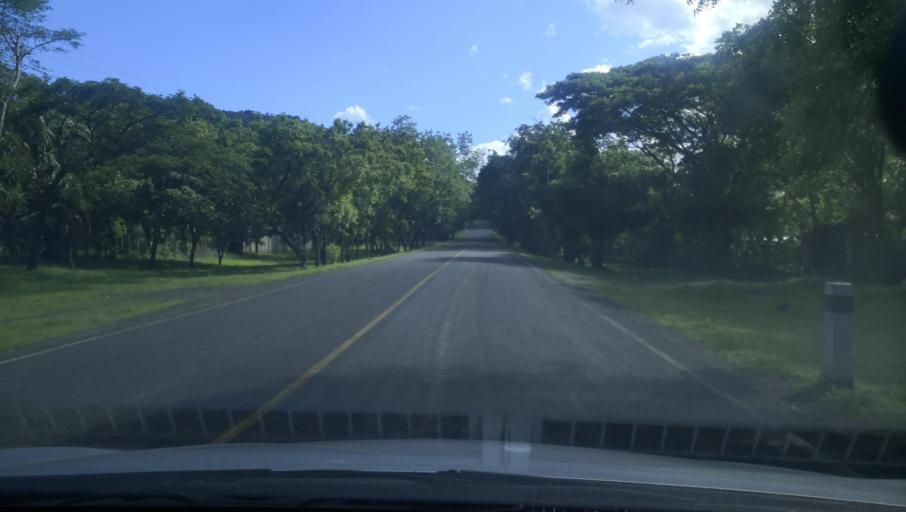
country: NI
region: Madriz
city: Somoto
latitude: 13.4679
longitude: -86.6324
